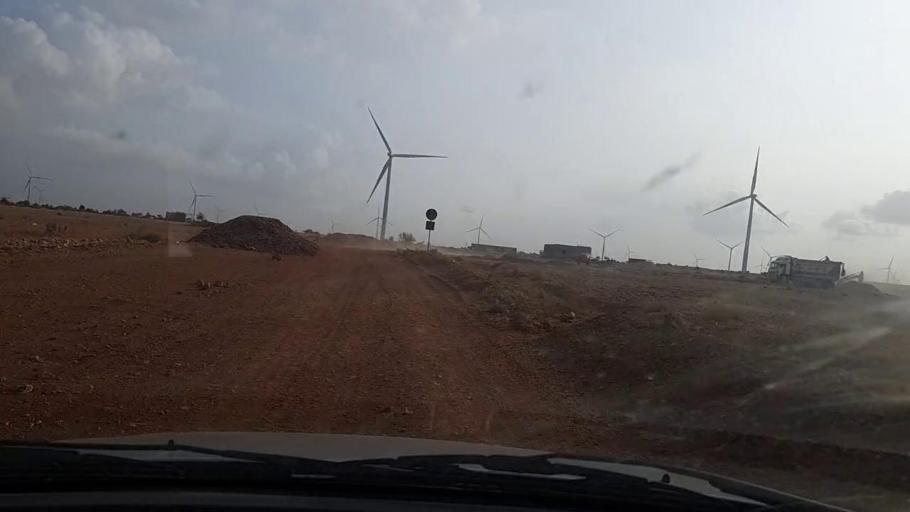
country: PK
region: Sindh
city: Thatta
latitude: 25.0482
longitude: 67.8664
